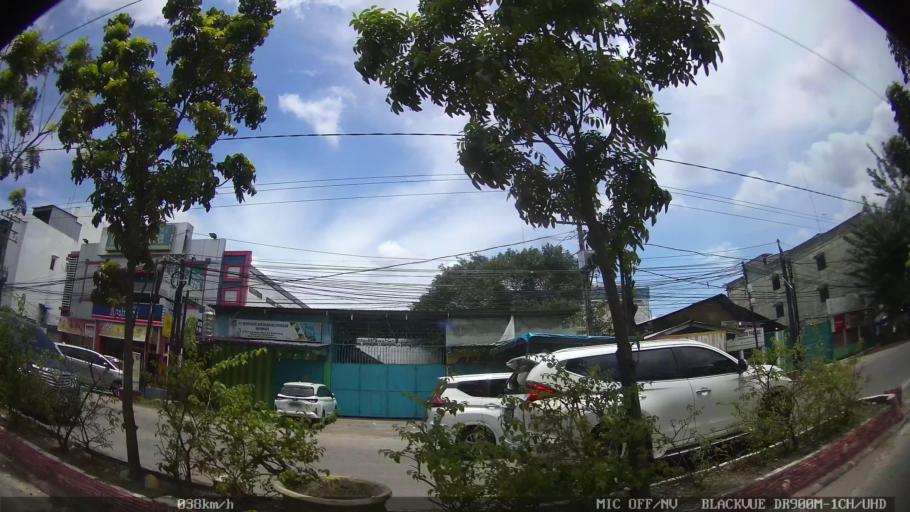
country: ID
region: North Sumatra
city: Medan
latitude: 3.6210
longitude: 98.6808
